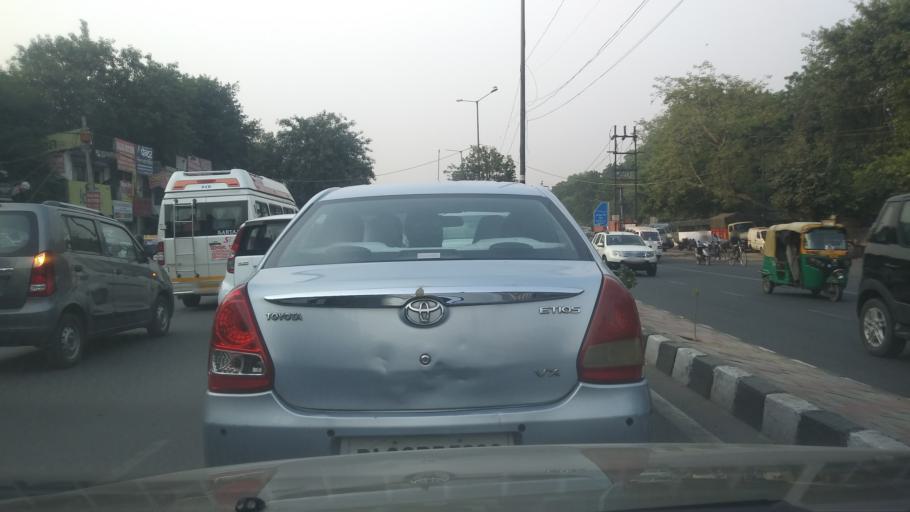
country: IN
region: Uttar Pradesh
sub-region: Gautam Buddha Nagar
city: Noida
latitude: 28.5375
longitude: 77.2670
